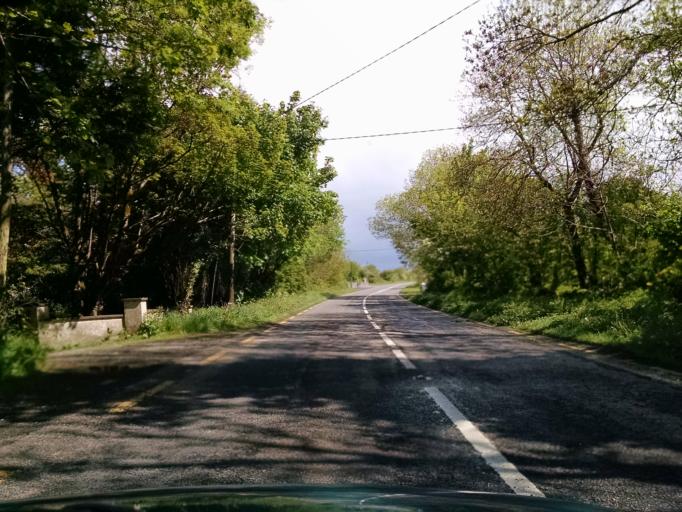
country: IE
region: Connaught
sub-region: County Galway
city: Oranmore
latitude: 53.1961
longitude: -8.8905
